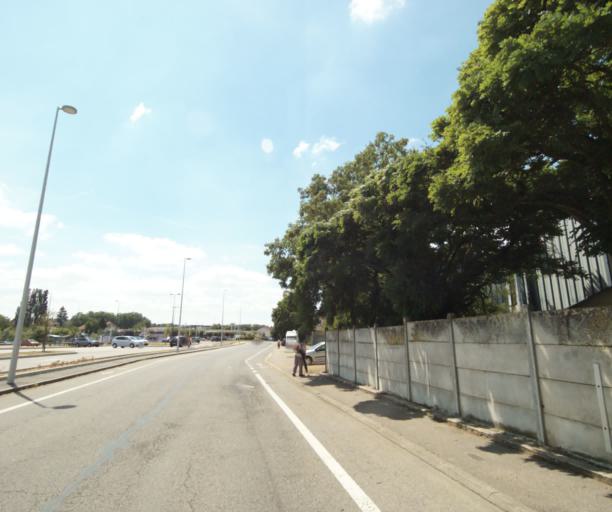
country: FR
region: Lorraine
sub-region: Departement de Meurthe-et-Moselle
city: Luneville
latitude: 48.5991
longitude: 6.4941
